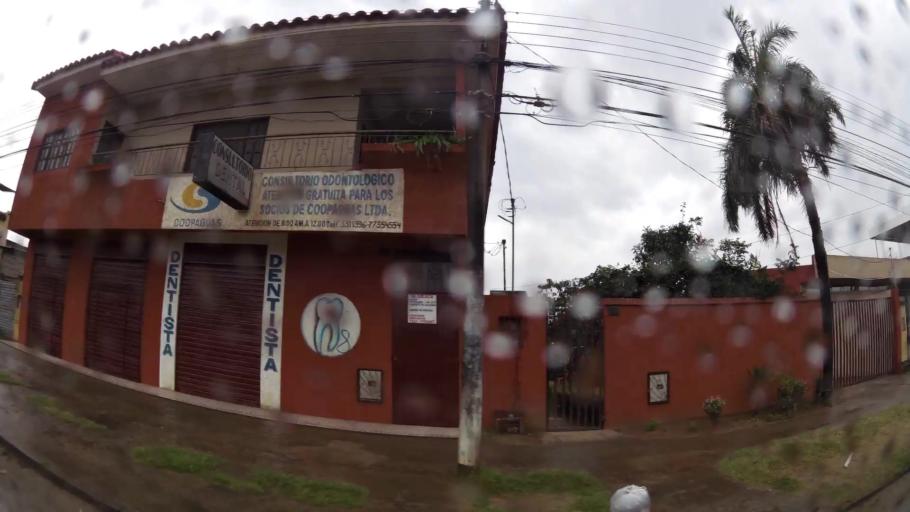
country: BO
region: Santa Cruz
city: Santa Cruz de la Sierra
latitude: -17.8072
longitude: -63.1283
